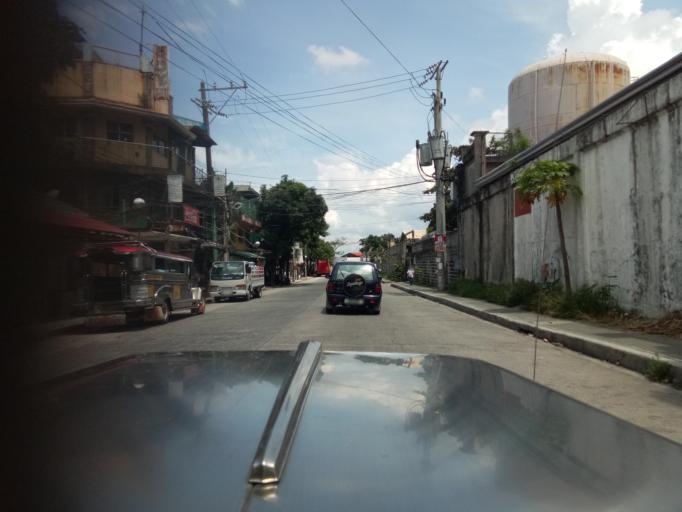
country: PH
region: Calabarzon
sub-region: Province of Cavite
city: Bulihan
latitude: 14.2858
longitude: 120.9973
